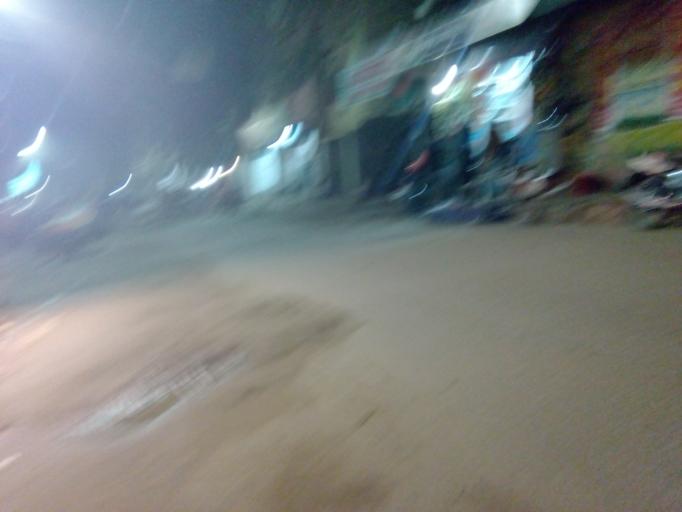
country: BD
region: Dhaka
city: Paltan
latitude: 23.7485
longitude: 90.4285
